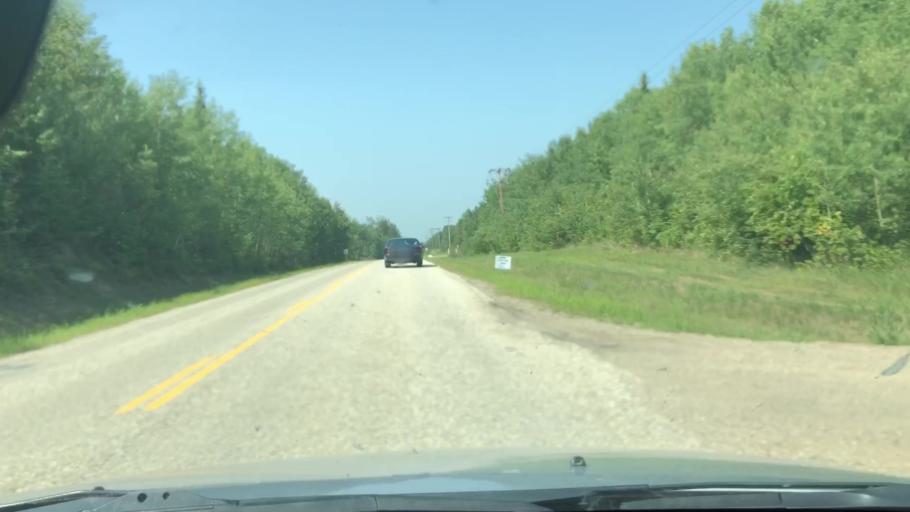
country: CA
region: Alberta
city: Devon
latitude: 53.4252
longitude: -113.7842
